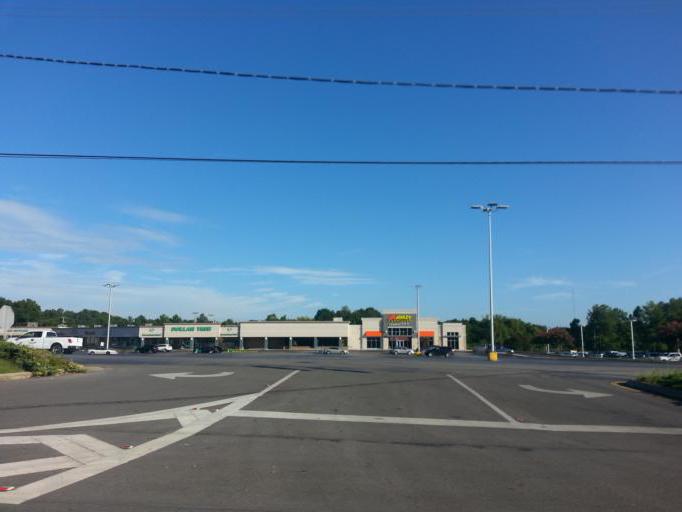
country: US
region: Alabama
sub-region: Lauderdale County
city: East Florence
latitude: 34.8216
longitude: -87.6520
